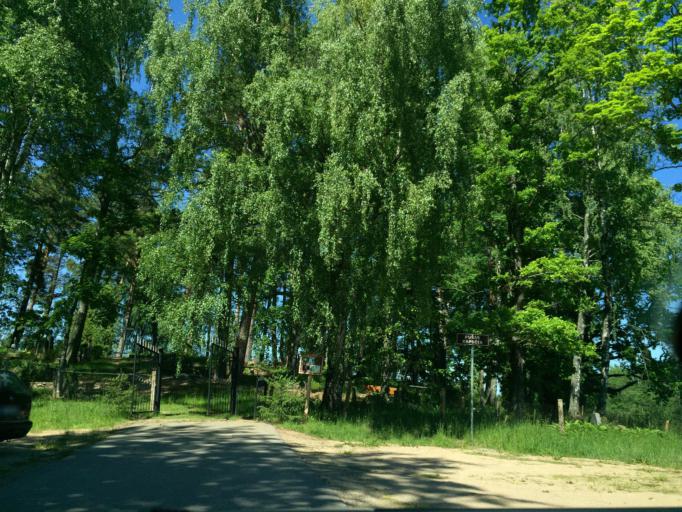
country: LV
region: Preilu Rajons
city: Jaunaglona
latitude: 56.2353
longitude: 27.2412
